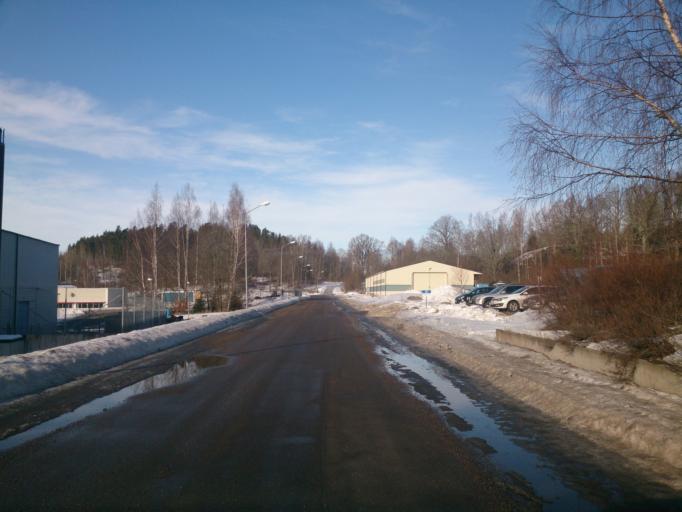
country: SE
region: OEstergoetland
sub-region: Atvidabergs Kommun
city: Atvidaberg
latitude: 58.2118
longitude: 15.9909
